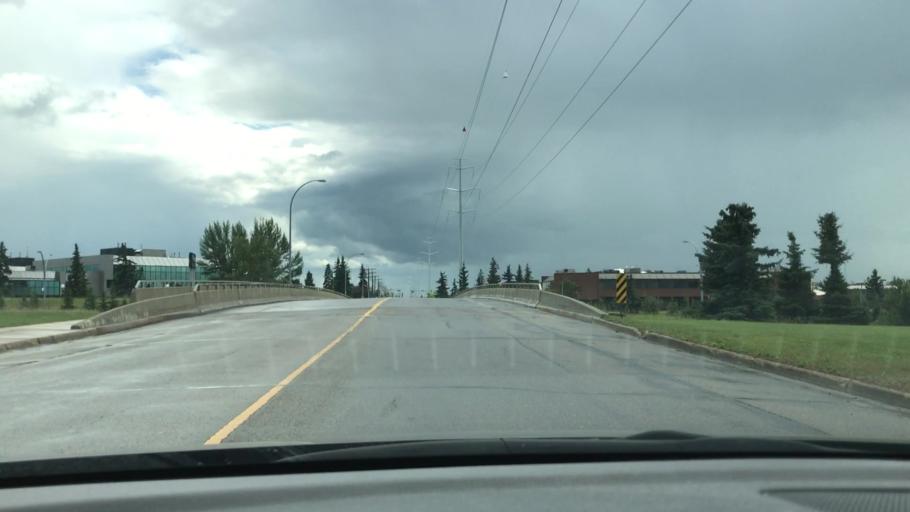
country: CA
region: Alberta
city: Edmonton
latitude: 53.4817
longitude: -113.4793
